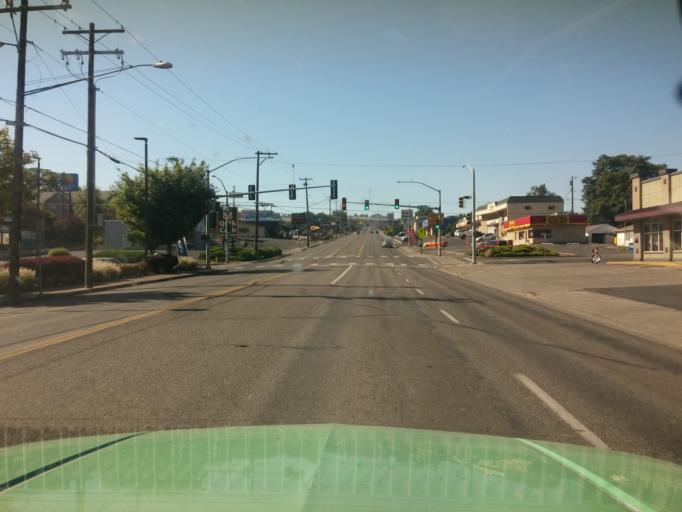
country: US
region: Idaho
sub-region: Nez Perce County
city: Lewiston
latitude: 46.4129
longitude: -117.0018
